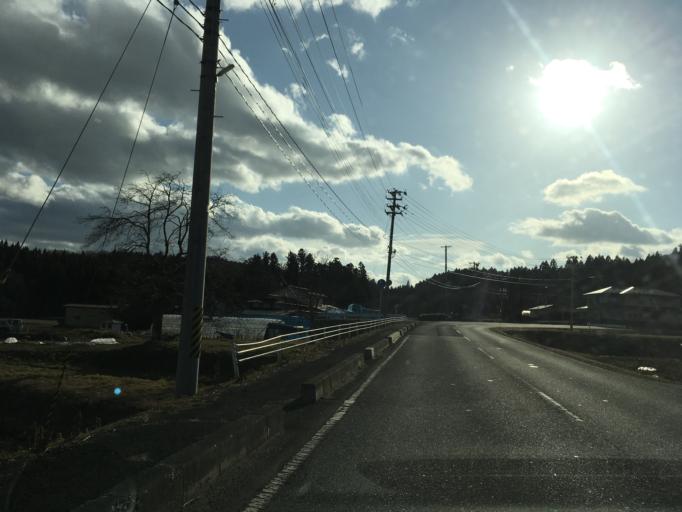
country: JP
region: Iwate
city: Ichinoseki
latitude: 38.8175
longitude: 140.9993
